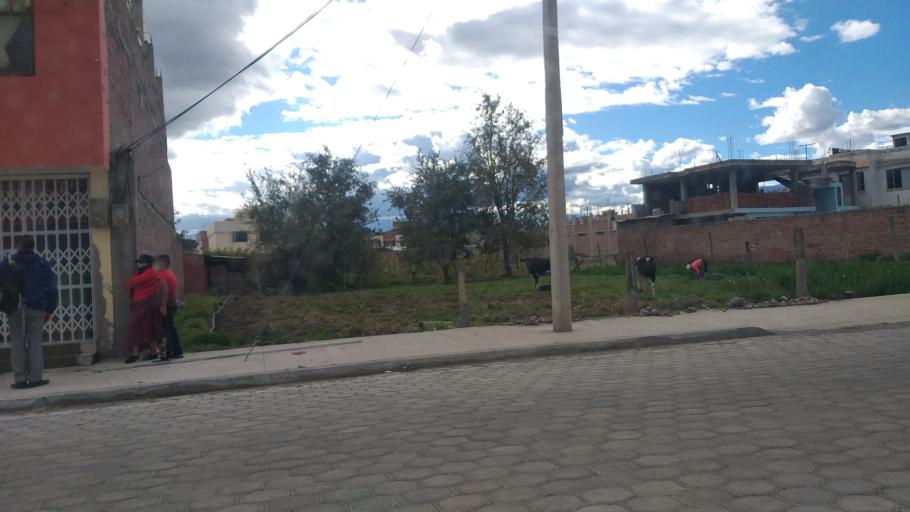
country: EC
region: Chimborazo
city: Riobamba
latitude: -1.6909
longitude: -78.6264
